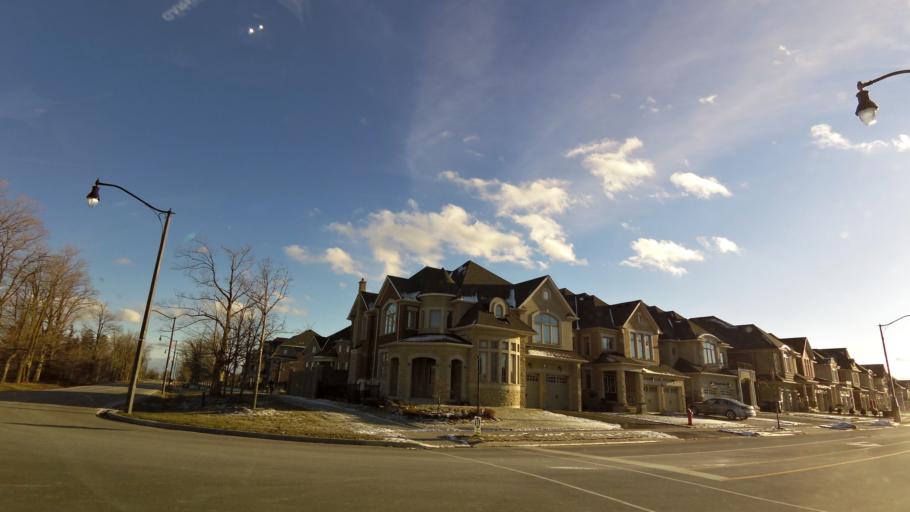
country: CA
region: Ontario
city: Brampton
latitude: 43.6665
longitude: -79.8055
